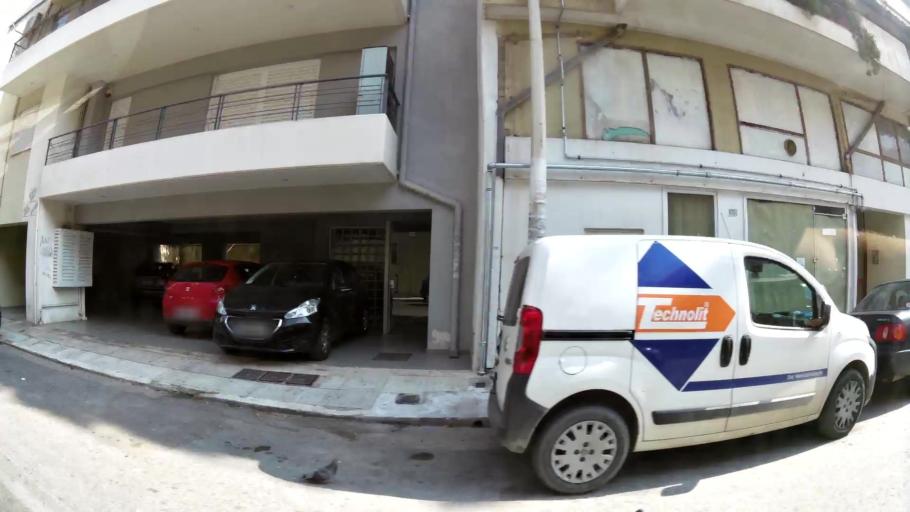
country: GR
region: Attica
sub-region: Nomarchia Athinas
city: Athens
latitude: 37.9943
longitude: 23.7176
